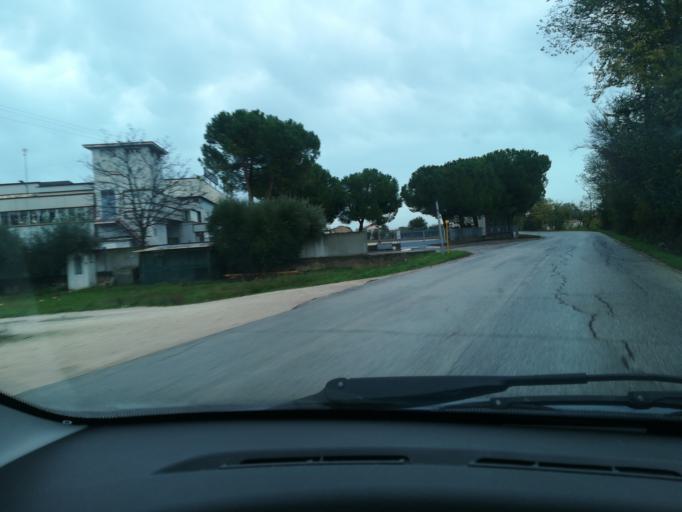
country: IT
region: The Marches
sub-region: Provincia di Macerata
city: Trodica
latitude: 43.2764
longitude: 13.6041
